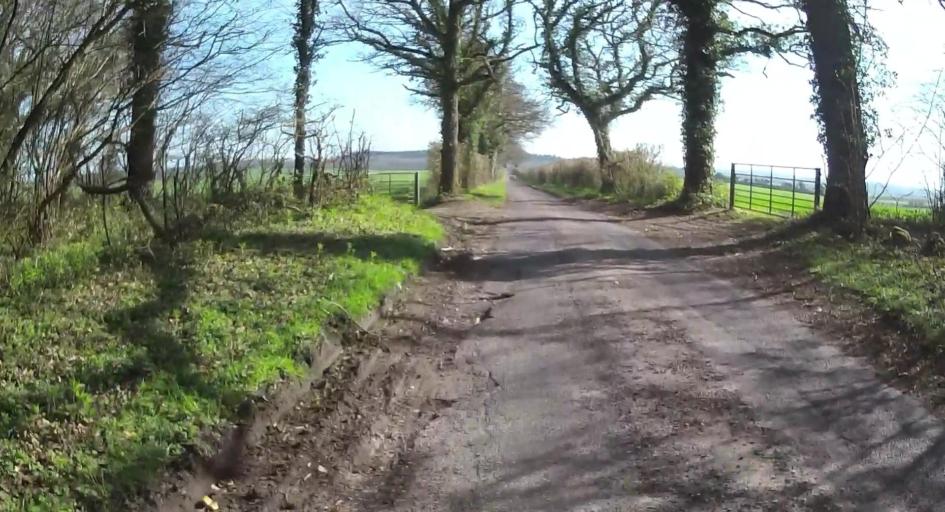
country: GB
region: England
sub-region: Hampshire
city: Highclere
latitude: 51.2533
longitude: -1.3675
